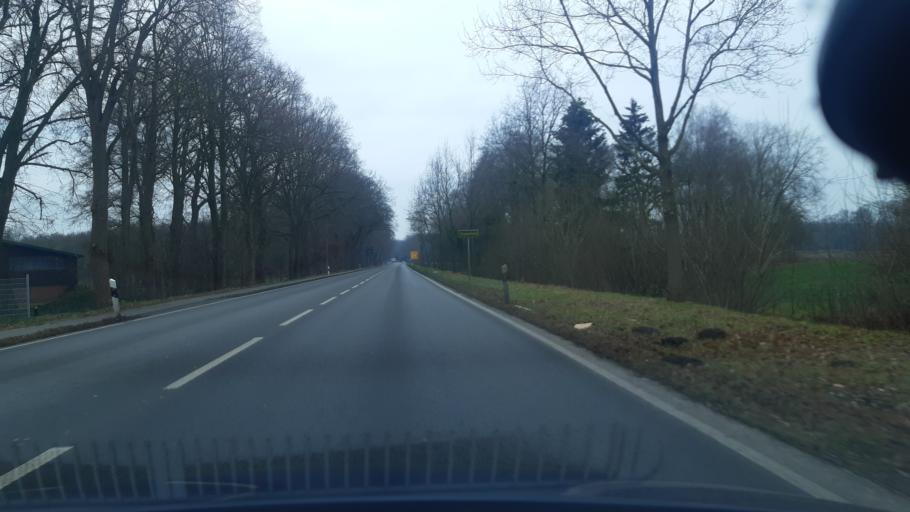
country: DE
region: Lower Saxony
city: Cloppenburg
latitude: 52.8250
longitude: 7.9971
